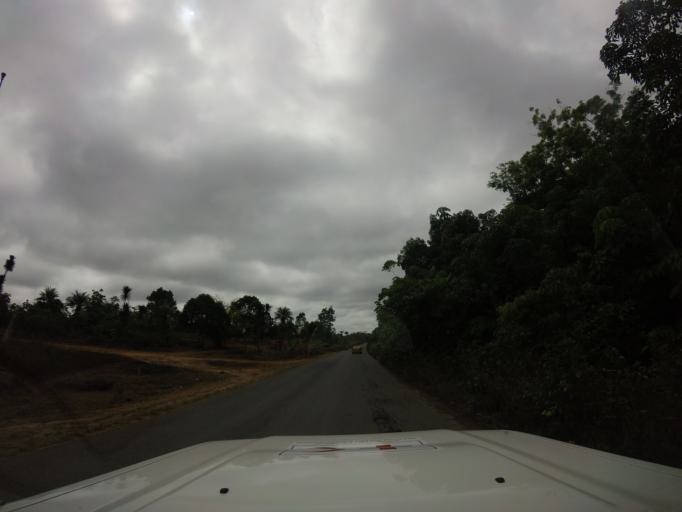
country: LR
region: Montserrado
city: Monrovia
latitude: 6.5590
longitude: -10.8691
